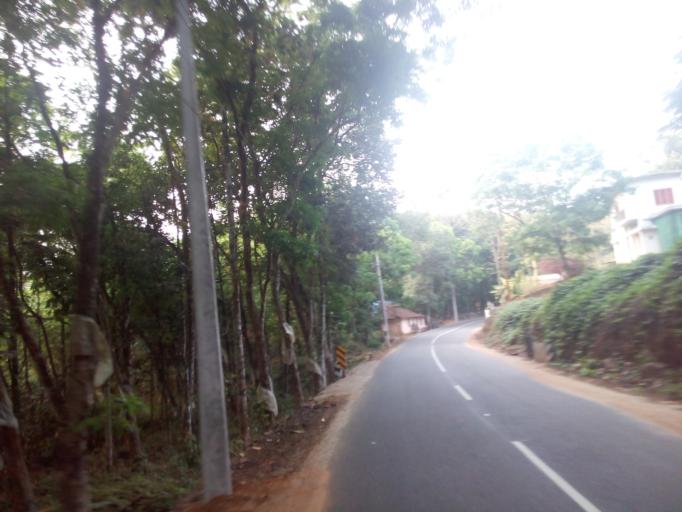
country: IN
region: Kerala
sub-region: Kottayam
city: Palackattumala
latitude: 9.8164
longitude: 76.6666
